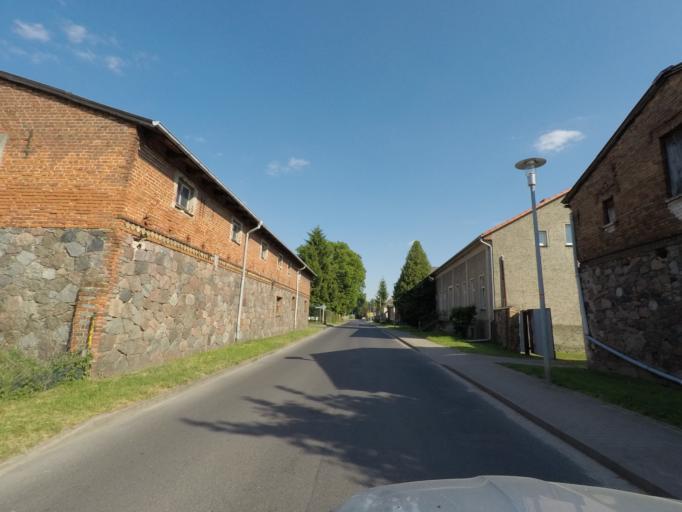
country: DE
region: Brandenburg
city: Werftpfuhl
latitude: 52.7381
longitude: 13.8365
